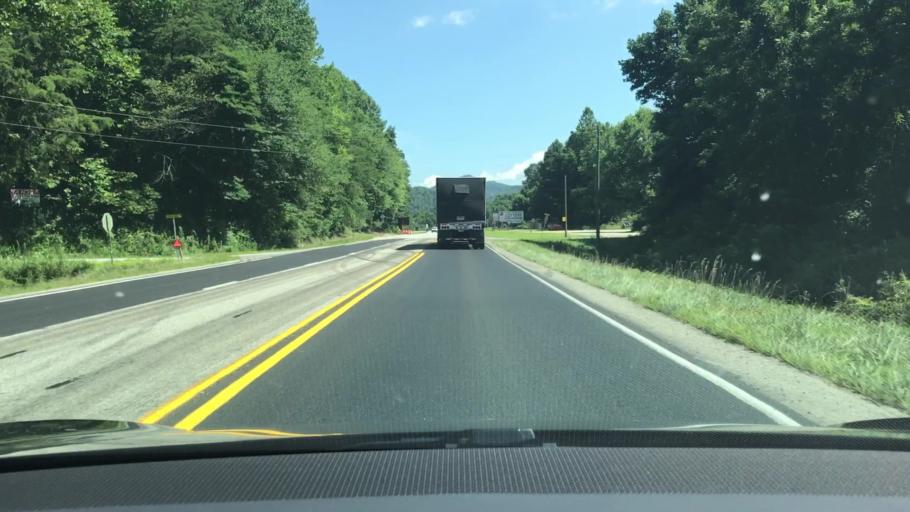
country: US
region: Georgia
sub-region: Rabun County
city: Mountain City
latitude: 34.9918
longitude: -83.3828
